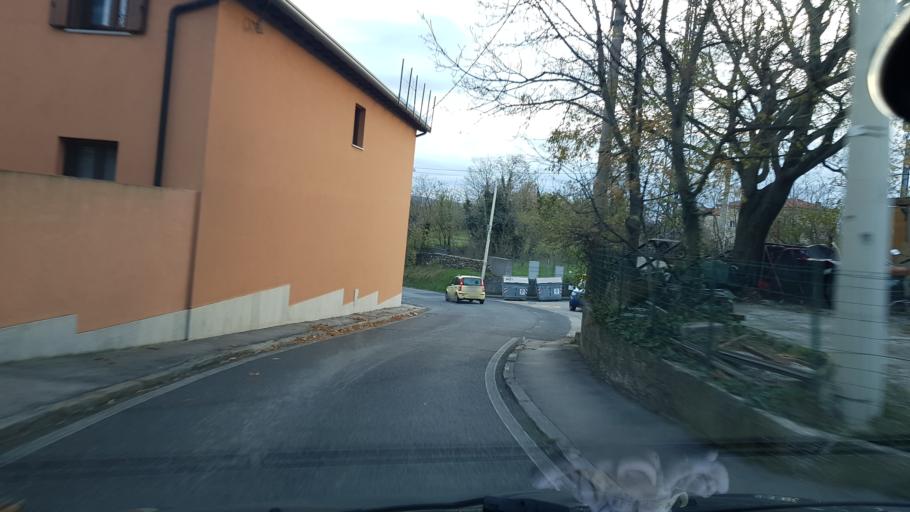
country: IT
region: Friuli Venezia Giulia
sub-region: Provincia di Trieste
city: Trieste
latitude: 45.6280
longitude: 13.8106
